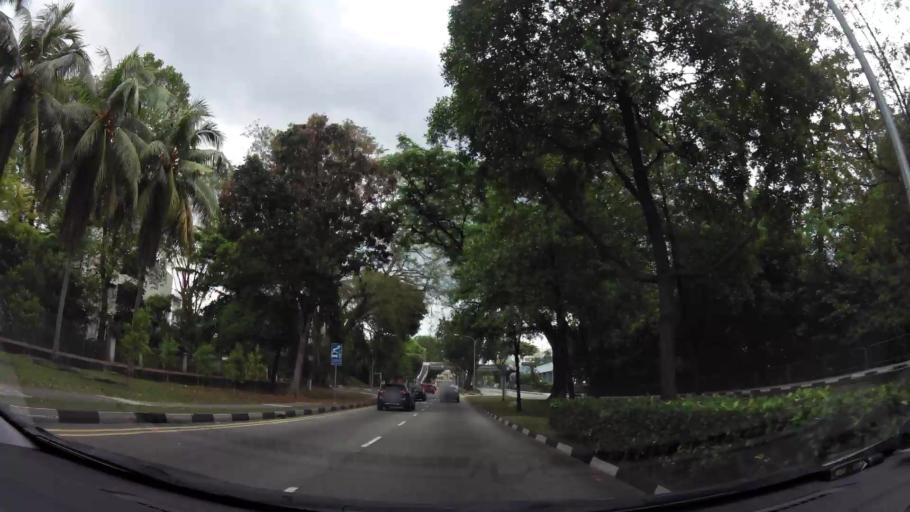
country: SG
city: Singapore
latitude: 1.3156
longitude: 103.8261
